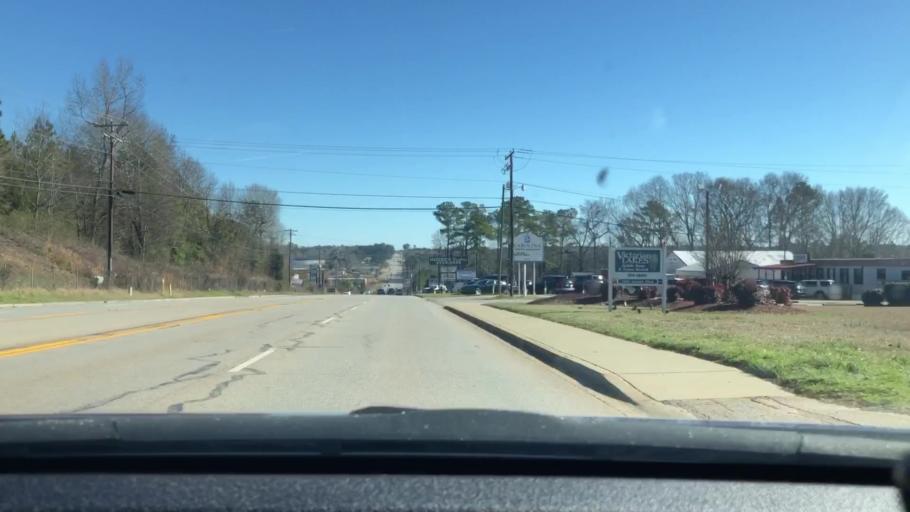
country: US
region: South Carolina
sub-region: Lexington County
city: Oak Grove
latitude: 34.0127
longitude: -81.1778
